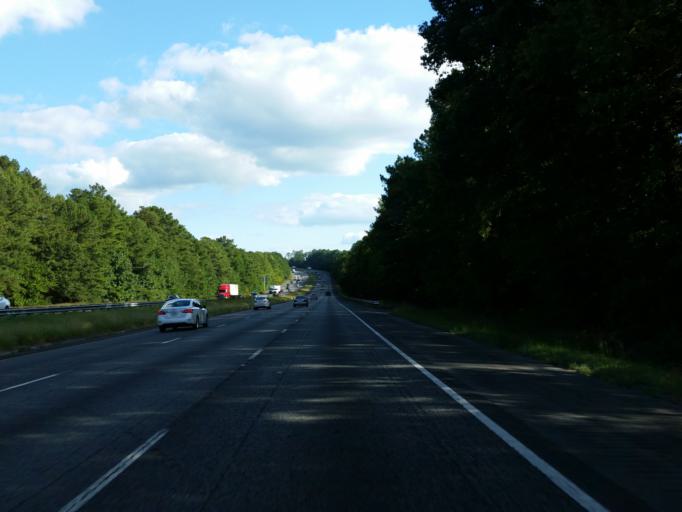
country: US
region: Georgia
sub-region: Butts County
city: Indian Springs
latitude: 33.1542
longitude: -84.0343
